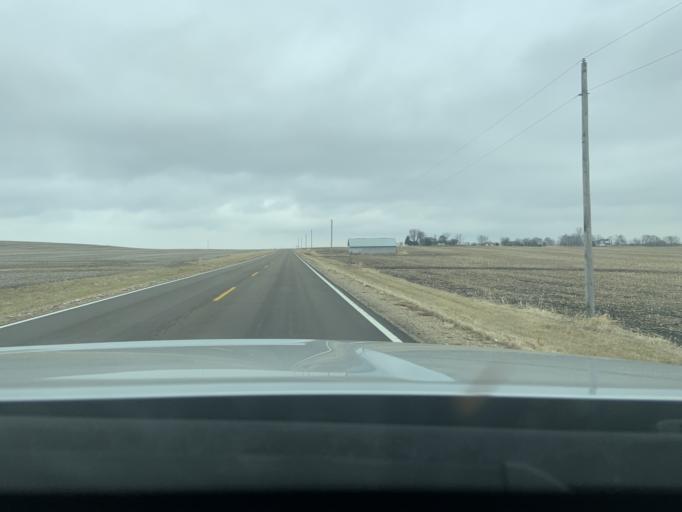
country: US
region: Illinois
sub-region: LaSalle County
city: Sheridan
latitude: 41.4673
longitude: -88.6156
